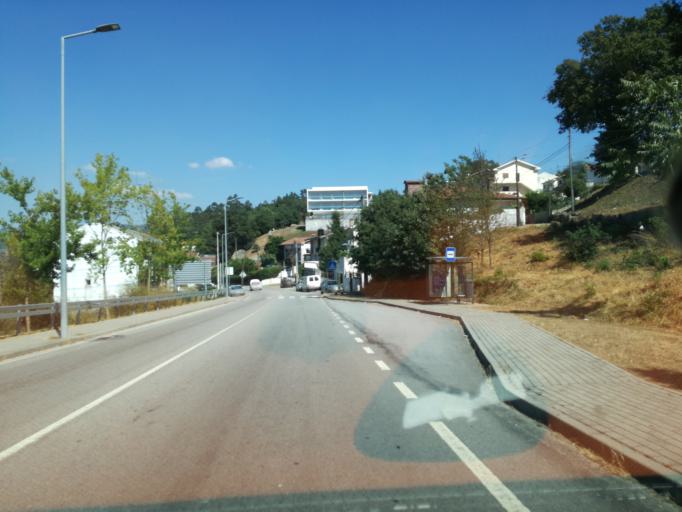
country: PT
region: Braga
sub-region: Guimaraes
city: Guimaraes
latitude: 41.4601
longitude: -8.2890
